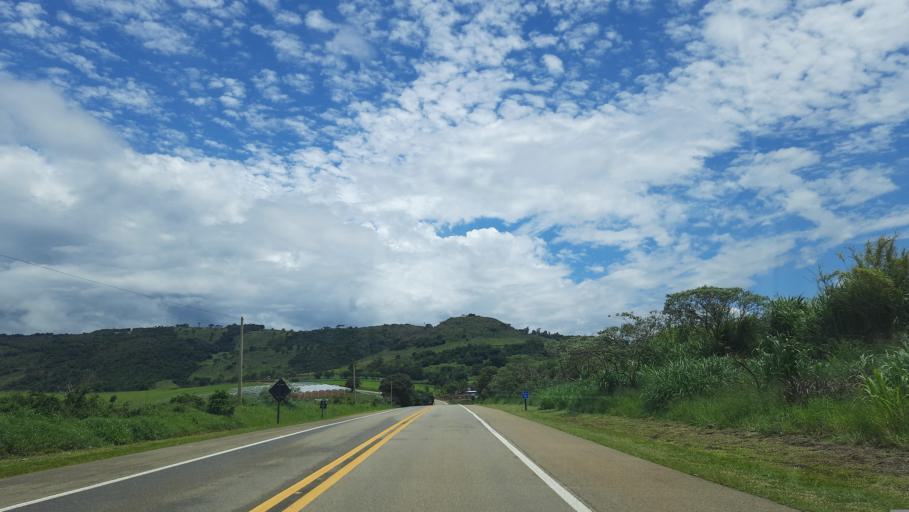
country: BR
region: Sao Paulo
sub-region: Vargem Grande Do Sul
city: Vargem Grande do Sul
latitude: -21.8166
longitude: -46.7847
